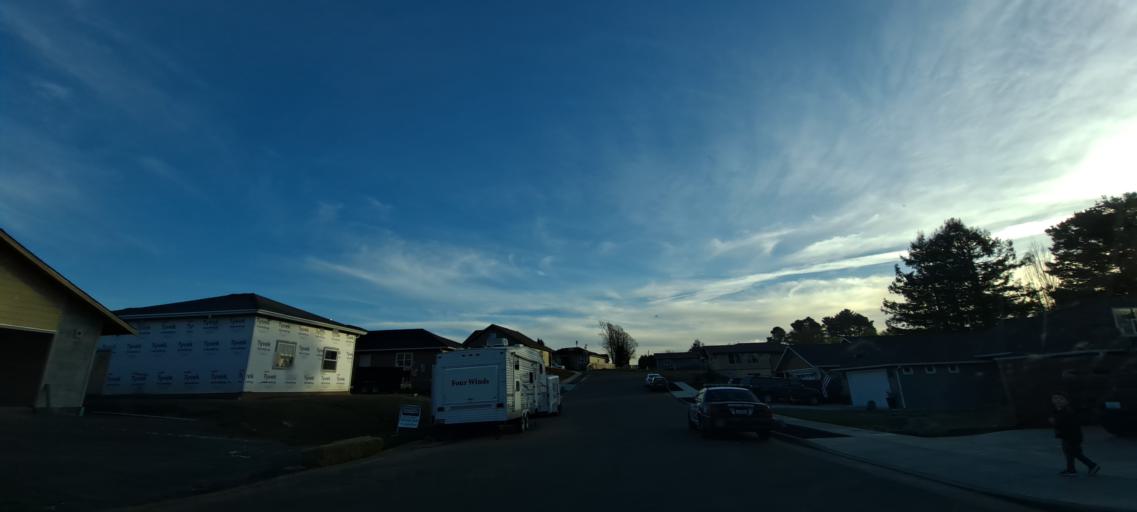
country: US
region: California
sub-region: Humboldt County
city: Fortuna
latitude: 40.5791
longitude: -124.1368
